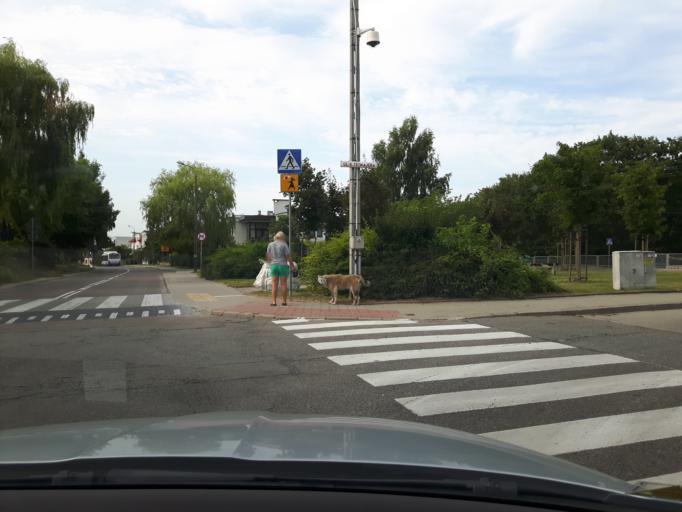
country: PL
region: Pomeranian Voivodeship
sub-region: Gdynia
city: Gdynia
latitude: 54.4991
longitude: 18.5492
